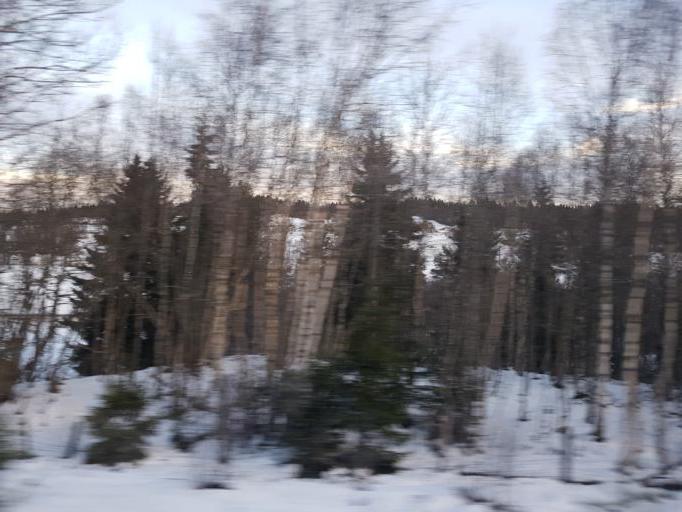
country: NO
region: Sor-Trondelag
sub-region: Rennebu
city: Berkak
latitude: 62.8688
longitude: 10.0526
